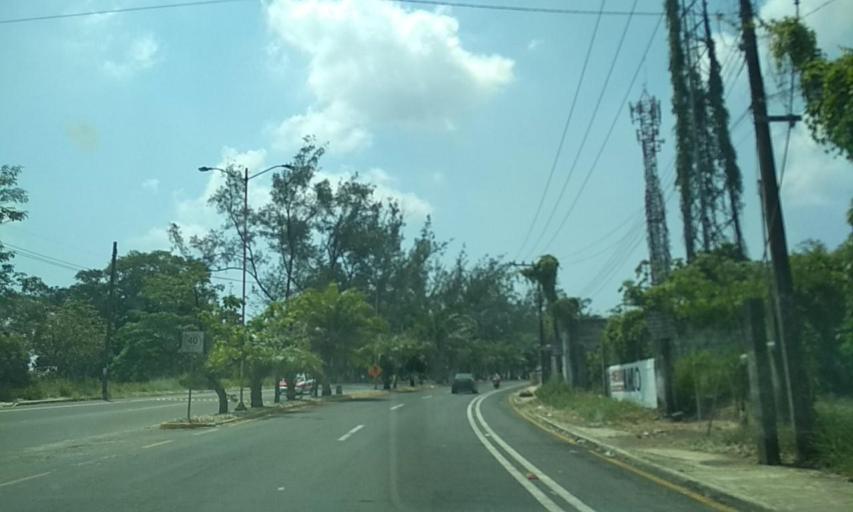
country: MX
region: Veracruz
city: Las Choapas
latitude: 17.9319
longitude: -94.0981
